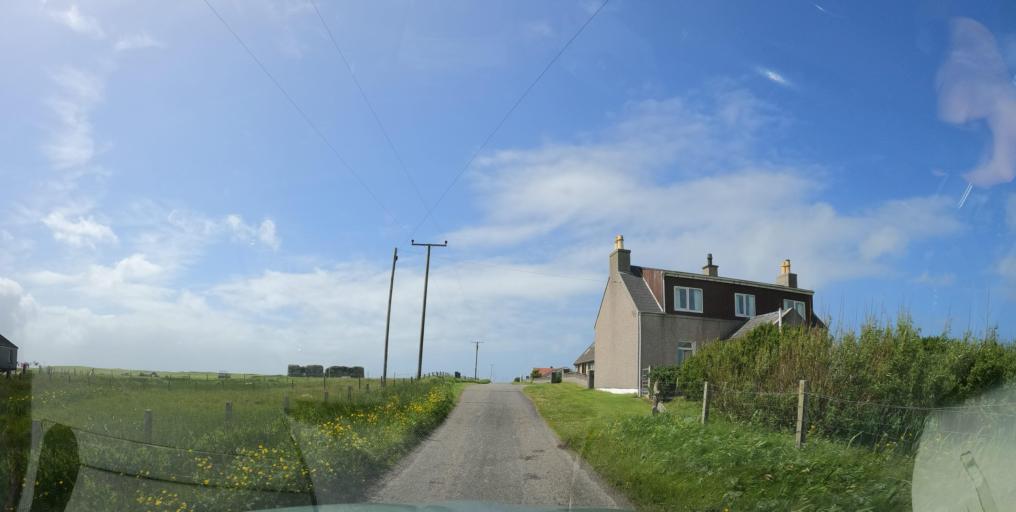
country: GB
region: Scotland
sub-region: Eilean Siar
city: Isle of South Uist
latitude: 57.1640
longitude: -7.3917
